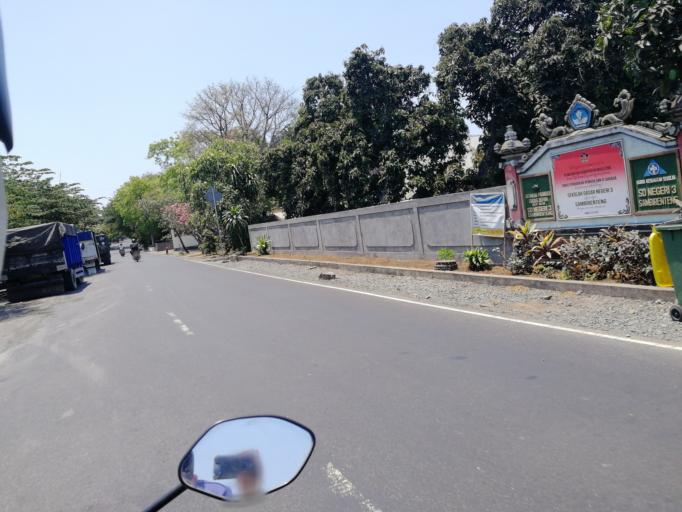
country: ID
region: Bali
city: Banjar Trunyan
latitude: -8.1526
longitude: 115.4153
